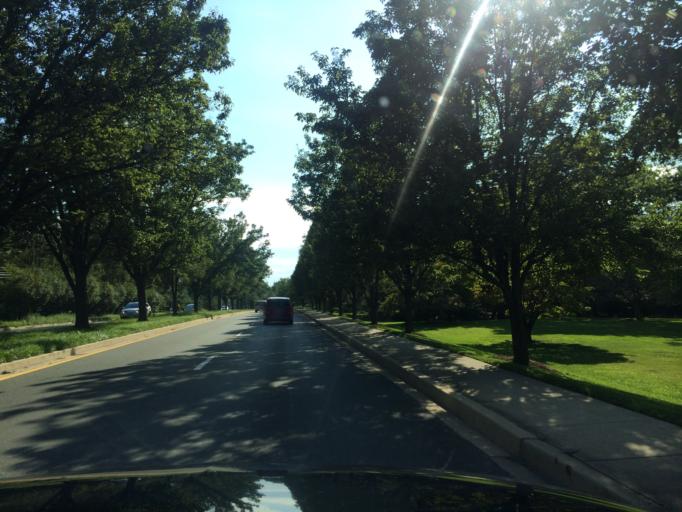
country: US
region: Maryland
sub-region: Montgomery County
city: Rossmoor
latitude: 39.1082
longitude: -77.0818
